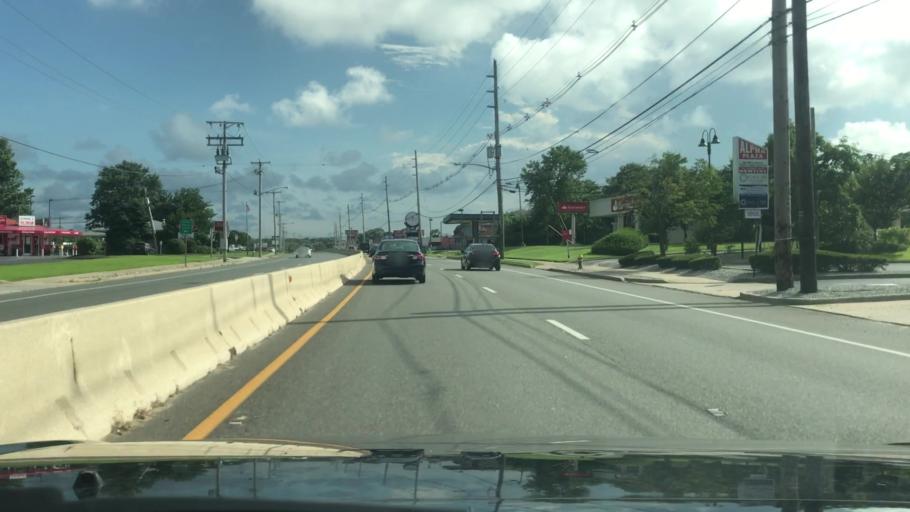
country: US
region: New Jersey
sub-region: Ocean County
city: Leisure Village East
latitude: 40.0141
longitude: -74.1461
